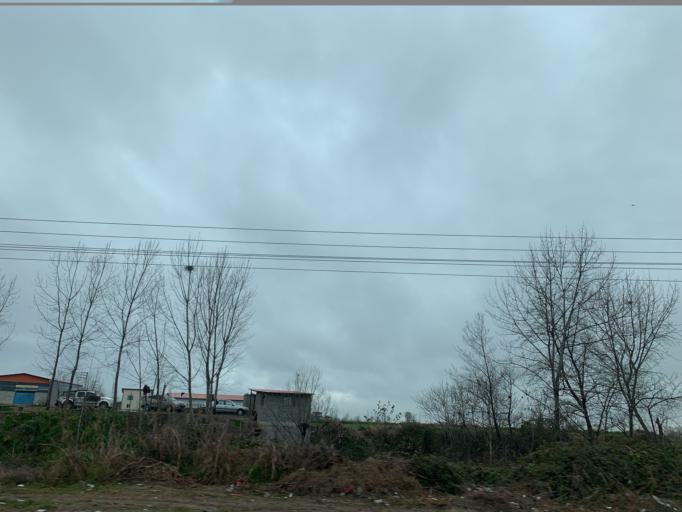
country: IR
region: Mazandaran
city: Amol
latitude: 36.4174
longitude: 52.3491
